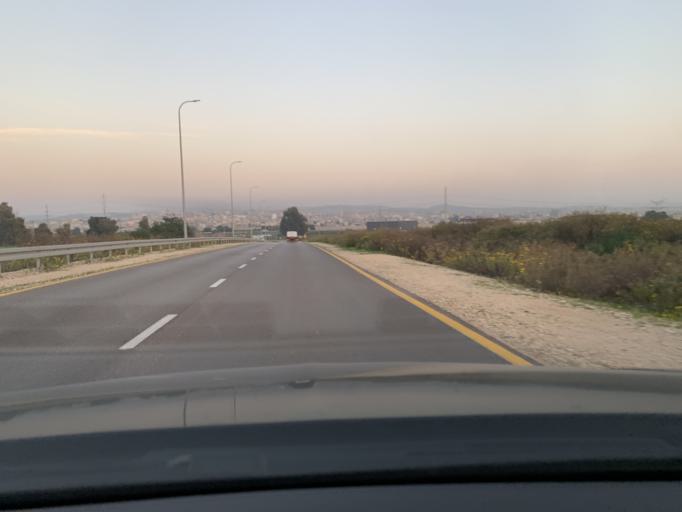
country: PS
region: West Bank
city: Qalqilyah
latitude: 32.1934
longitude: 34.9478
